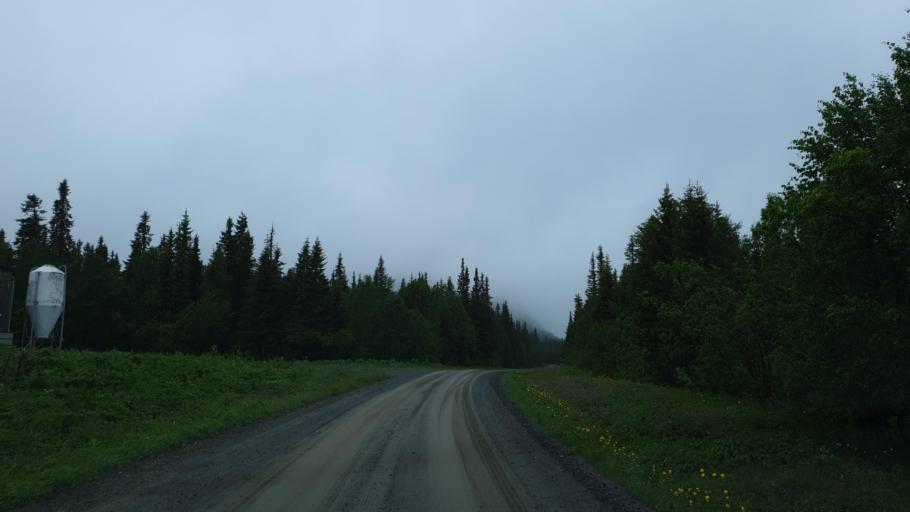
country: SE
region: Vaesterbotten
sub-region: Vilhelmina Kommun
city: Sjoberg
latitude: 65.2774
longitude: 15.8959
